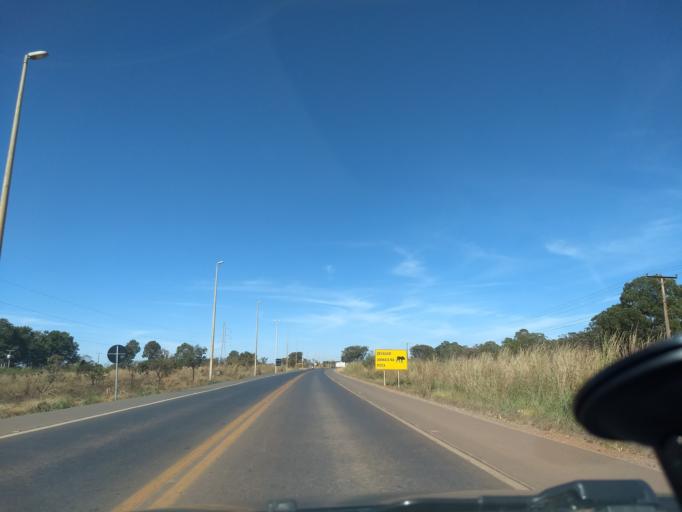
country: BR
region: Federal District
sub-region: Brasilia
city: Brasilia
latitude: -15.7752
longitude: -48.0463
